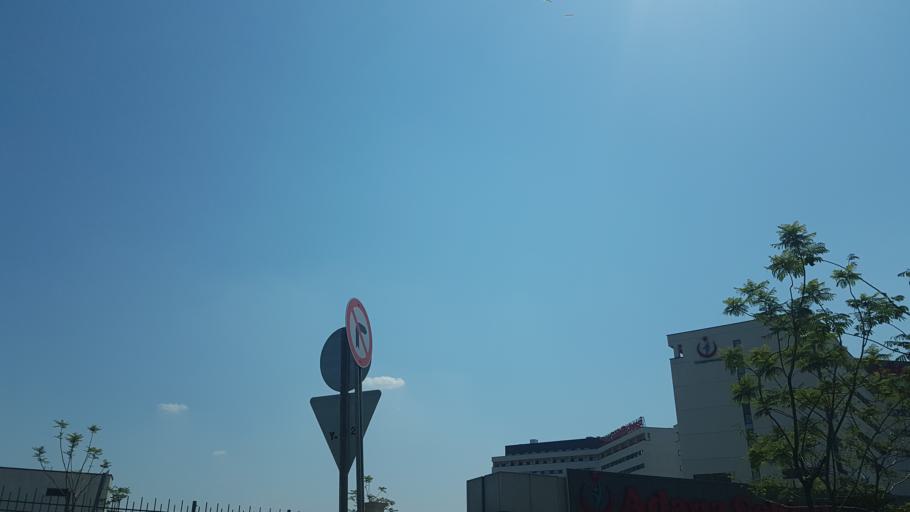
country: TR
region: Adana
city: Adana
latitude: 37.0307
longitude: 35.3504
